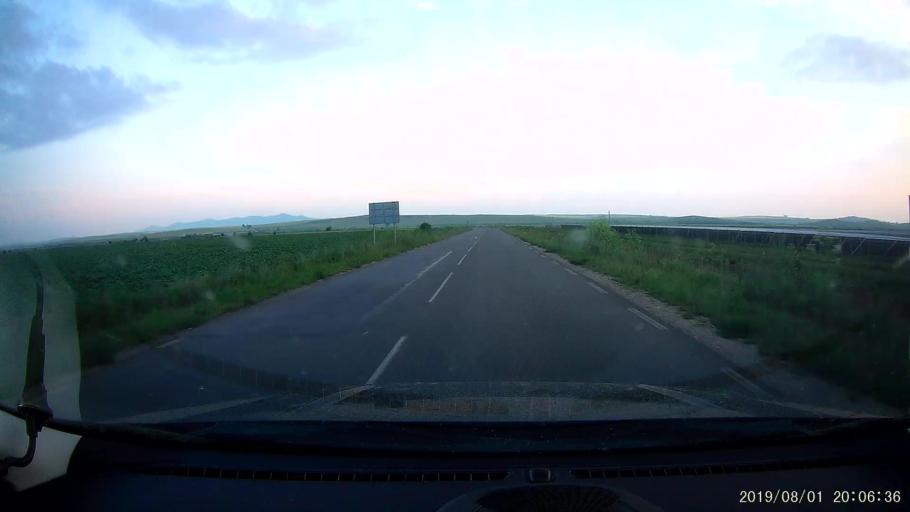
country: BG
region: Yambol
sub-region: Obshtina Yambol
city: Yambol
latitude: 42.5328
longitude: 26.5568
